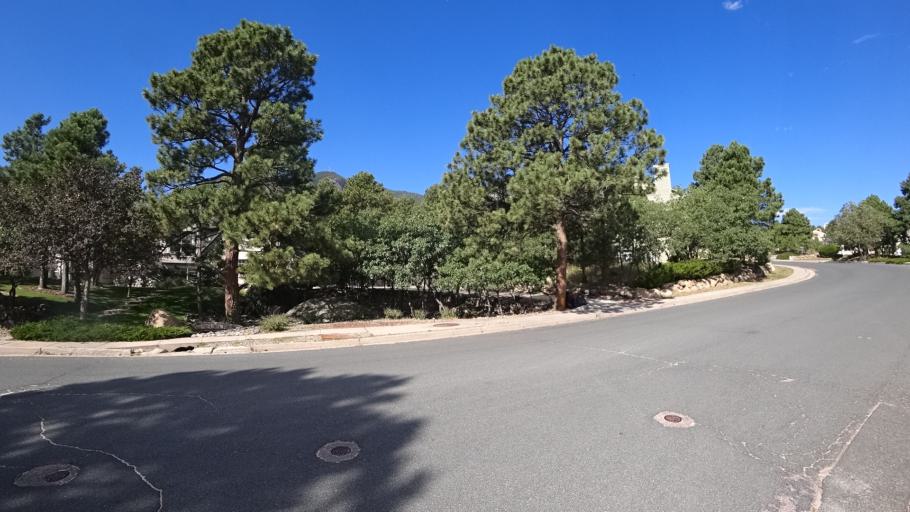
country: US
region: Colorado
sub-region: El Paso County
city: Fort Carson
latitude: 38.7622
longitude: -104.8335
